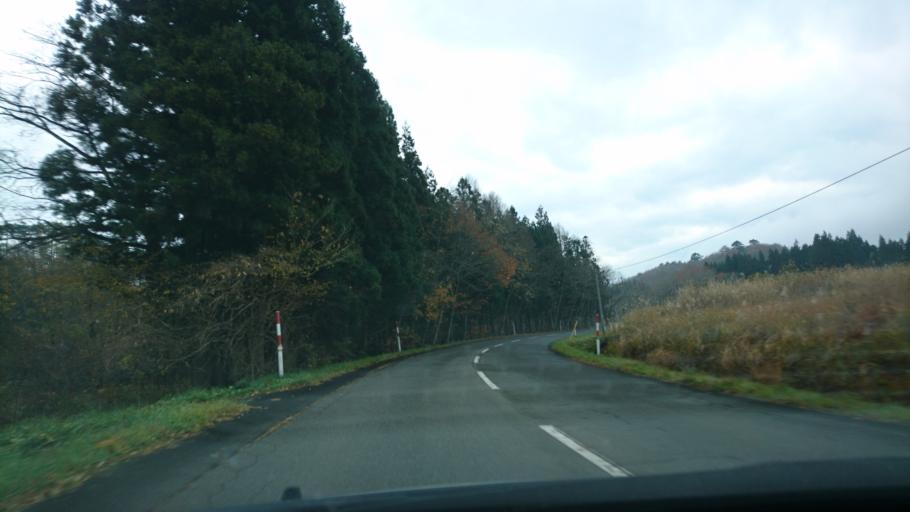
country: JP
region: Iwate
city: Ichinoseki
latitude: 38.9430
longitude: 140.9258
